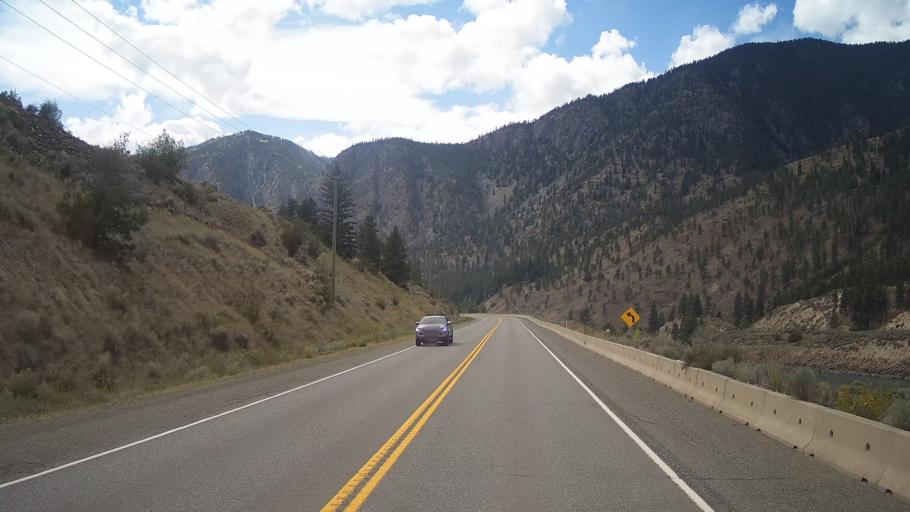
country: CA
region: British Columbia
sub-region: Thompson-Nicola Regional District
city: Ashcroft
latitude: 50.3942
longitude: -121.3882
